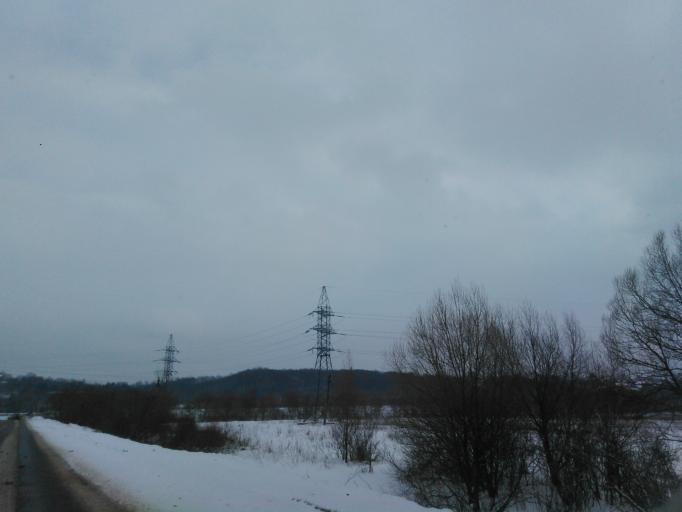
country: RU
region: Moskovskaya
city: Yakhroma
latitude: 56.2780
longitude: 37.4960
